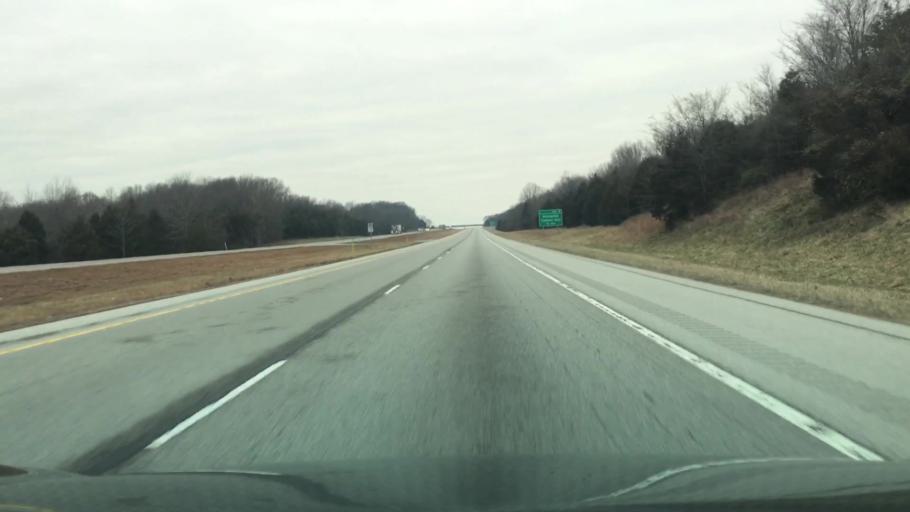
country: US
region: Illinois
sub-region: Johnson County
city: Goreville
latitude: 37.5228
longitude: -88.9150
